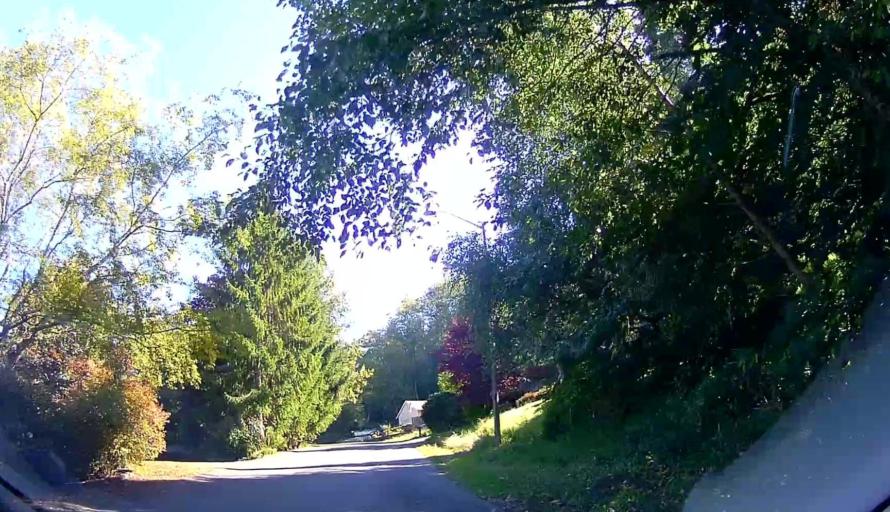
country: US
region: Washington
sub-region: Skagit County
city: Big Lake
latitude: 48.4325
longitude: -122.2780
